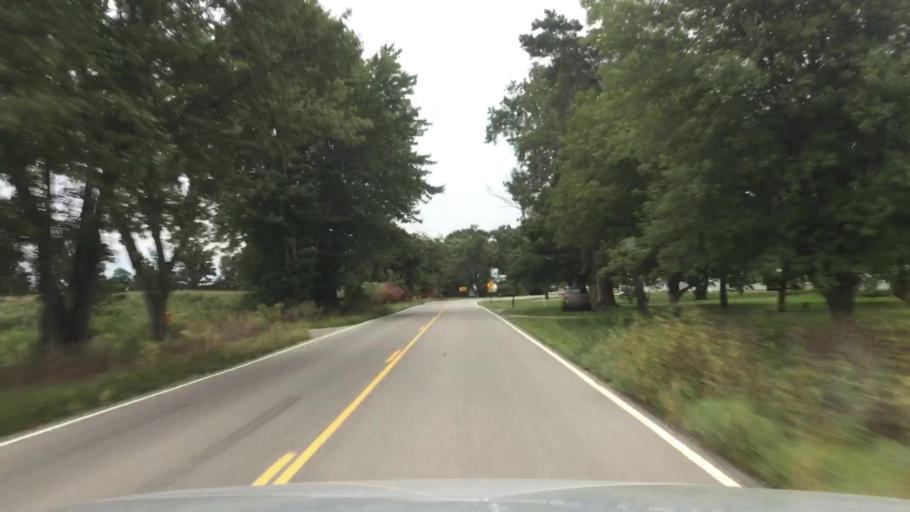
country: US
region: Michigan
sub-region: Washtenaw County
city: Milan
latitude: 42.0859
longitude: -83.7351
